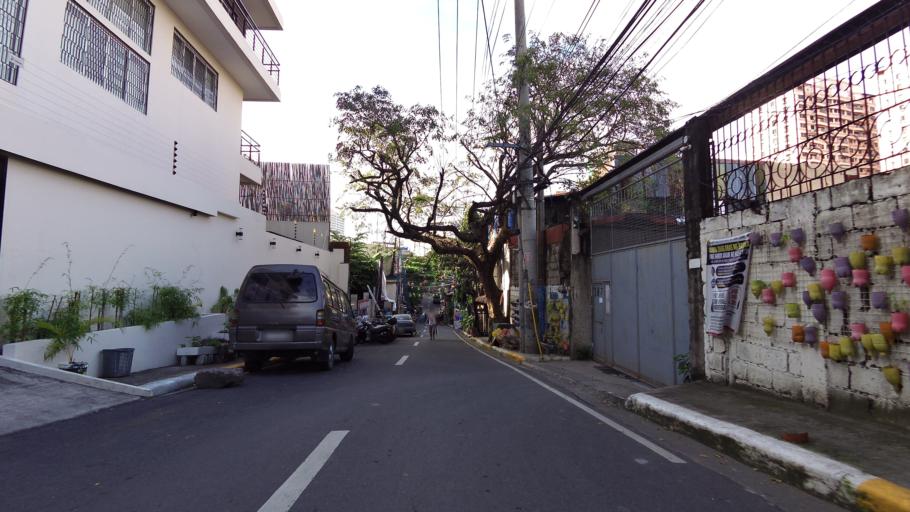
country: PH
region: Metro Manila
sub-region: San Juan
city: San Juan
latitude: 14.6081
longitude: 121.0339
